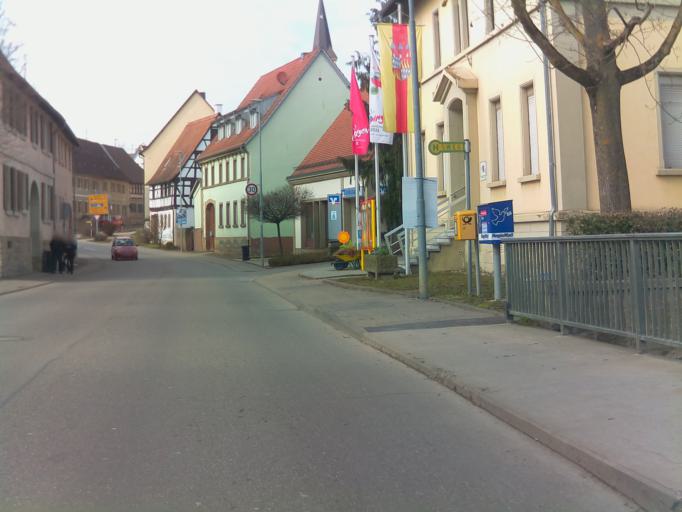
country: DE
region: Baden-Wuerttemberg
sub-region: Regierungsbezirk Stuttgart
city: Ittlingen
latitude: 49.1702
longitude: 8.9423
